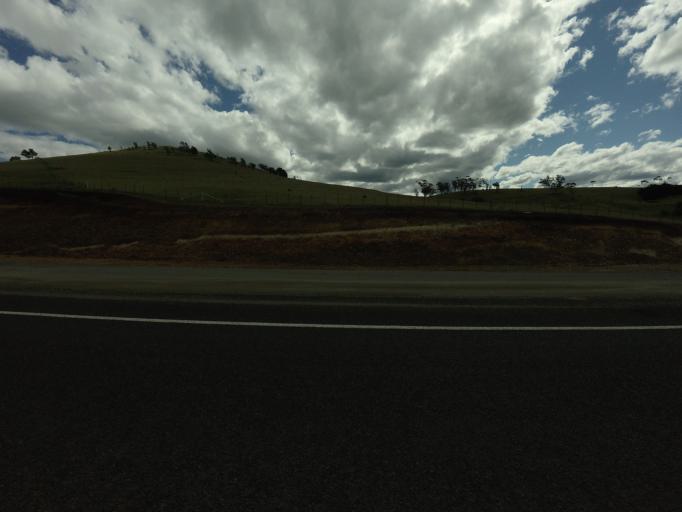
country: AU
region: Tasmania
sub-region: Brighton
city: Bridgewater
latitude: -42.2201
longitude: 147.4106
